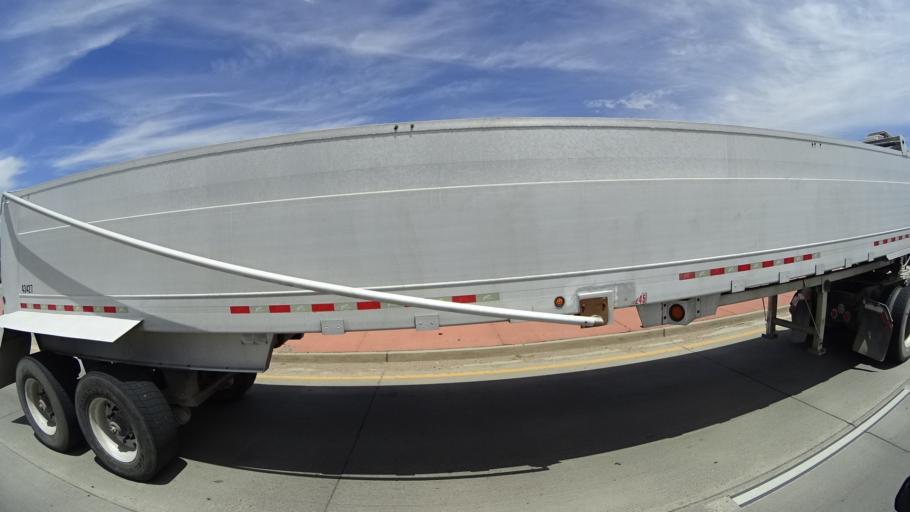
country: US
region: Colorado
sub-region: El Paso County
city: Security-Widefield
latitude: 38.7278
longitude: -104.7227
